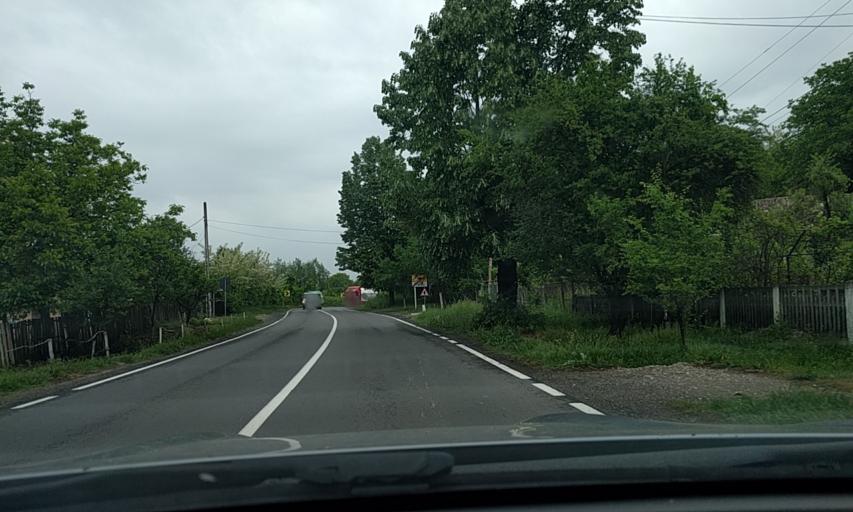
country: RO
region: Dambovita
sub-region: Comuna Branesti
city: Branesti
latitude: 45.0316
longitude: 25.4246
